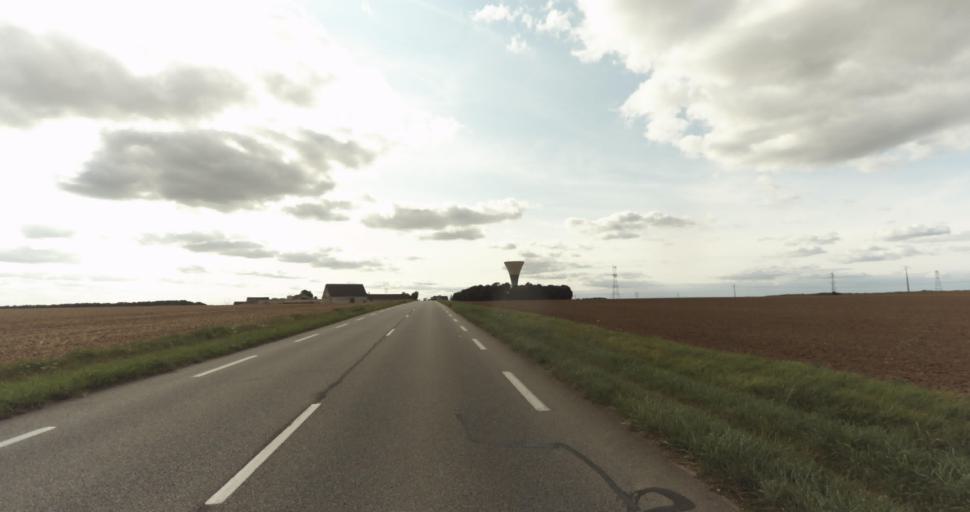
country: FR
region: Haute-Normandie
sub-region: Departement de l'Eure
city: Garennes-sur-Eure
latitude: 48.8907
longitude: 1.4358
